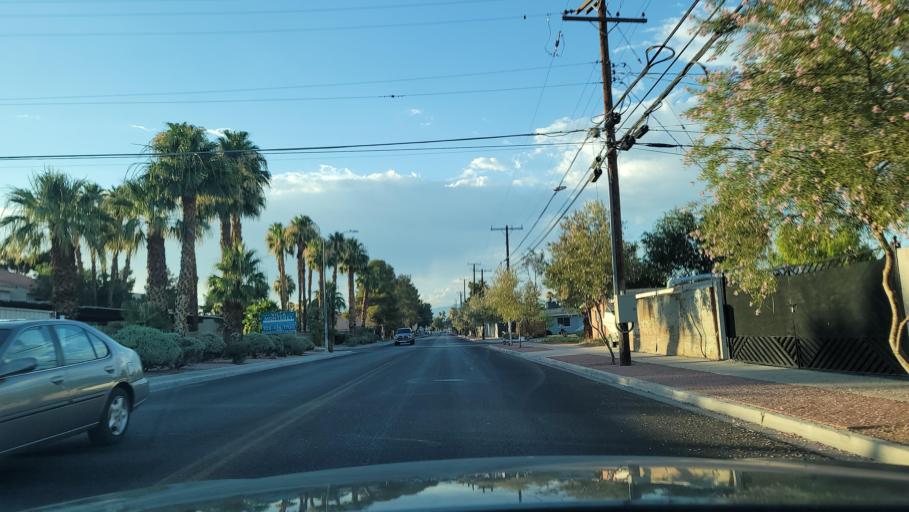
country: US
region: Nevada
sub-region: Clark County
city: Las Vegas
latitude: 36.1553
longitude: -115.1234
